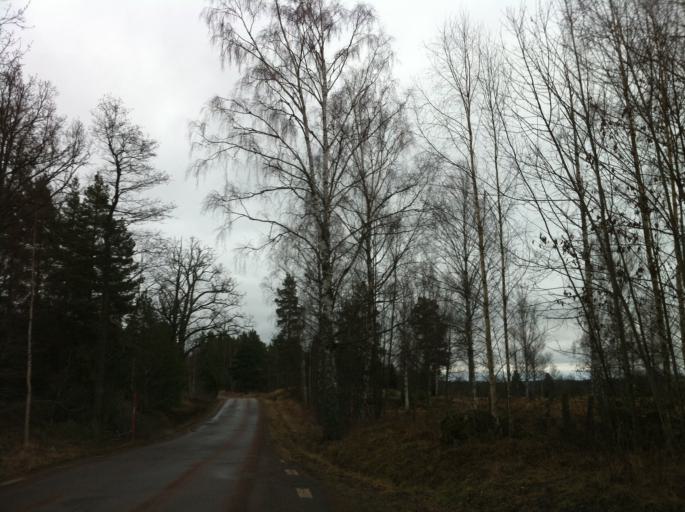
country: SE
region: Kalmar
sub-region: Vasterviks Kommun
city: Forserum
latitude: 57.9261
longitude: 16.5428
